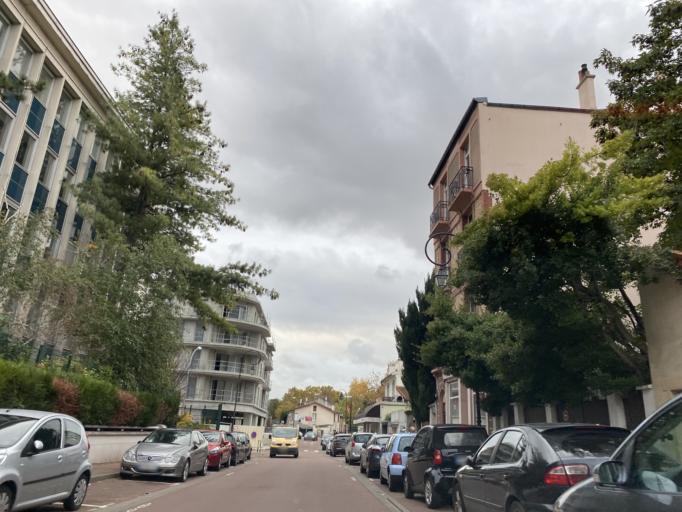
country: FR
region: Ile-de-France
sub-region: Departement des Hauts-de-Seine
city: Saint-Cloud
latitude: 48.8519
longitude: 2.2213
